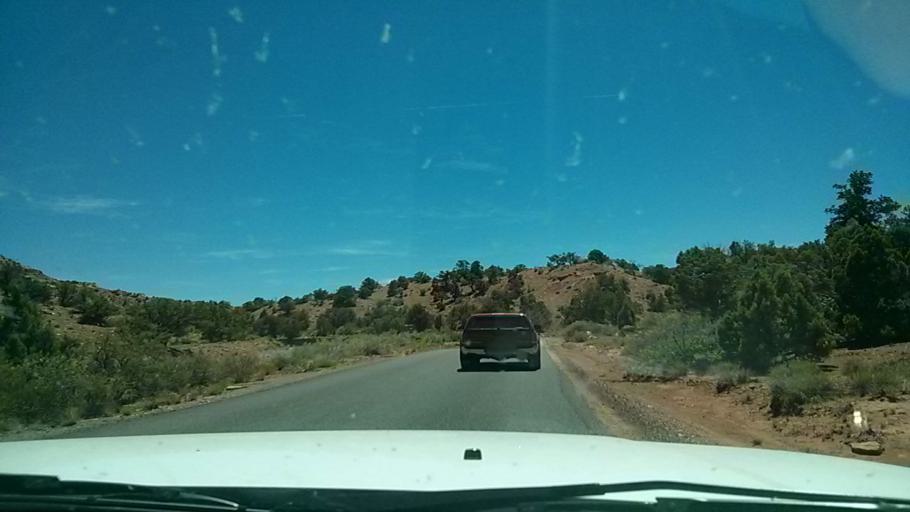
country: US
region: Utah
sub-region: Wayne County
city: Loa
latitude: 38.2404
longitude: -111.2243
